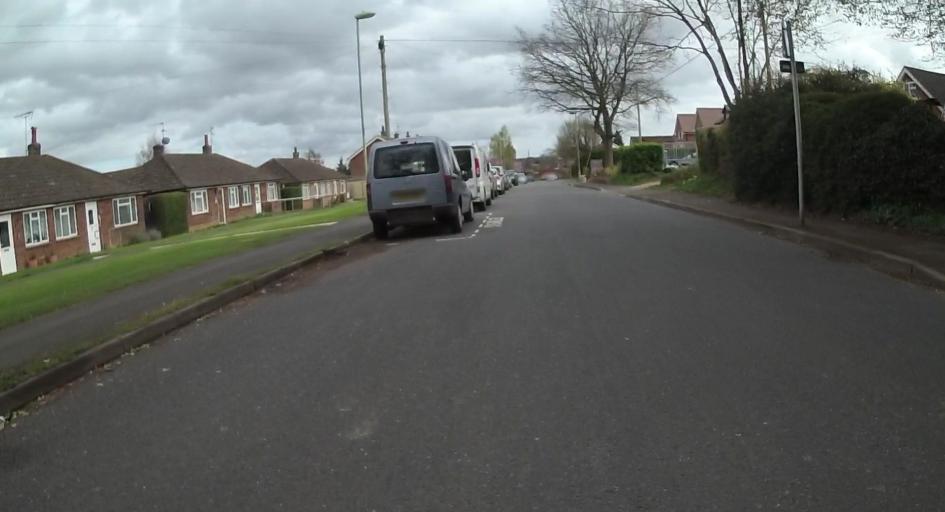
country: GB
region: England
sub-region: Hampshire
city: Alton
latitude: 51.1615
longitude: -0.9701
